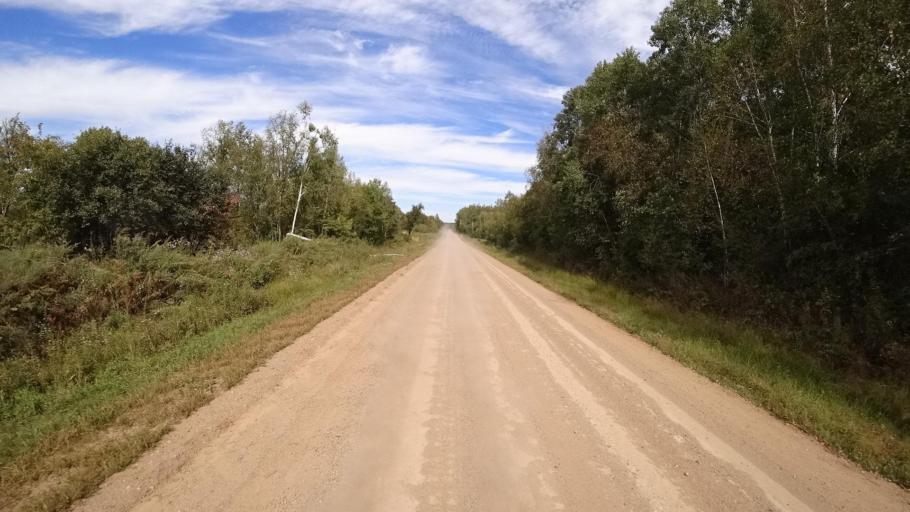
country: RU
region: Primorskiy
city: Yakovlevka
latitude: 44.5782
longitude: 133.5965
